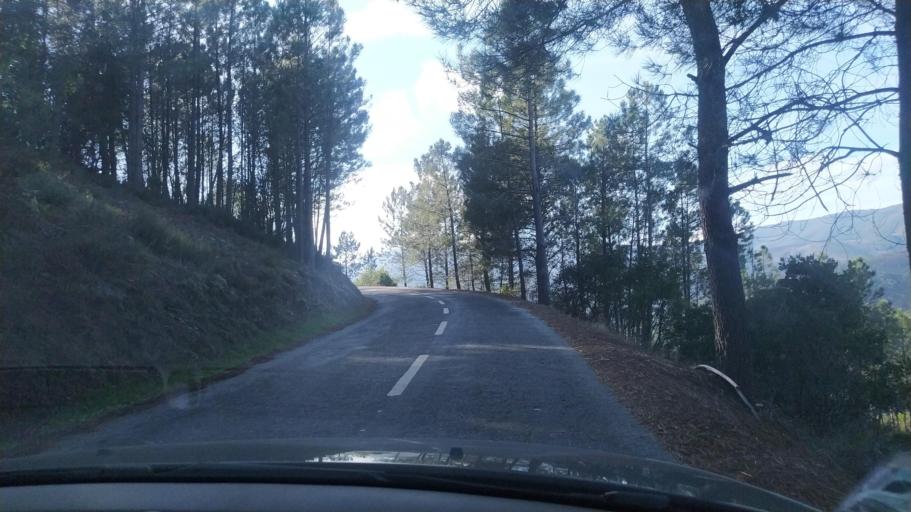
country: PT
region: Coimbra
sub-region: Oliveira do Hospital
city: Oliveira do Hospital
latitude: 40.2015
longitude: -7.7281
